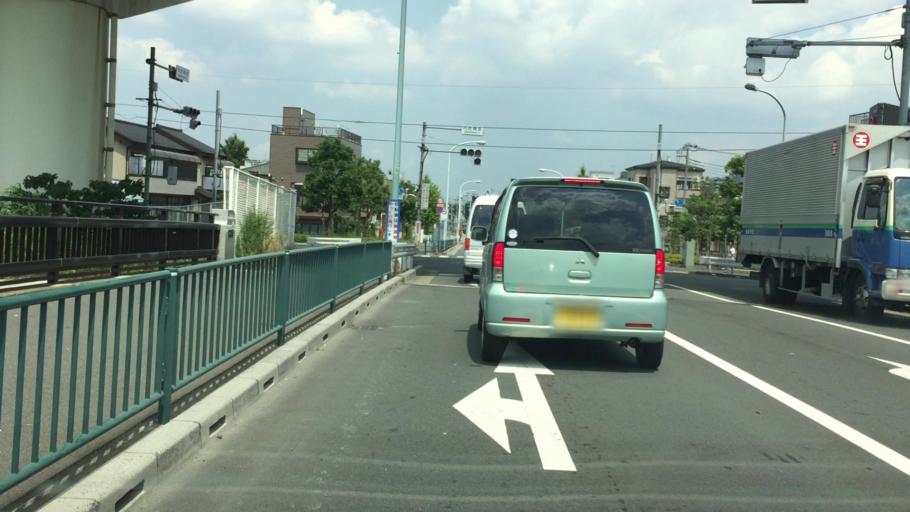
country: JP
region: Saitama
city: Yashio-shi
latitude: 35.7922
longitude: 139.8279
